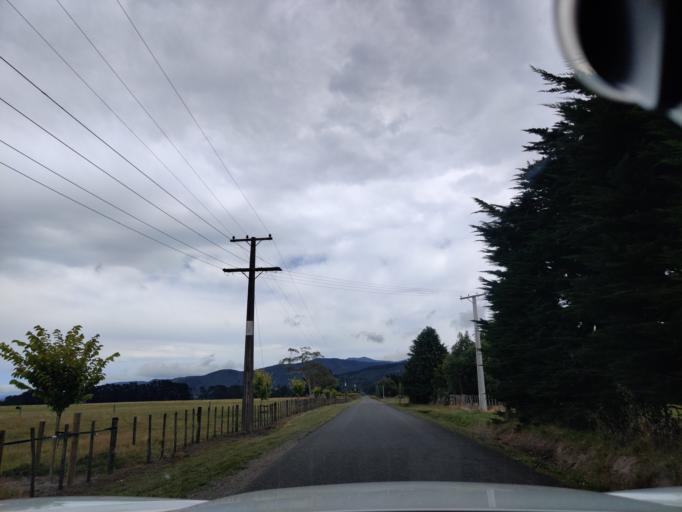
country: NZ
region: Wellington
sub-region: Masterton District
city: Masterton
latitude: -41.0364
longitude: 175.4455
